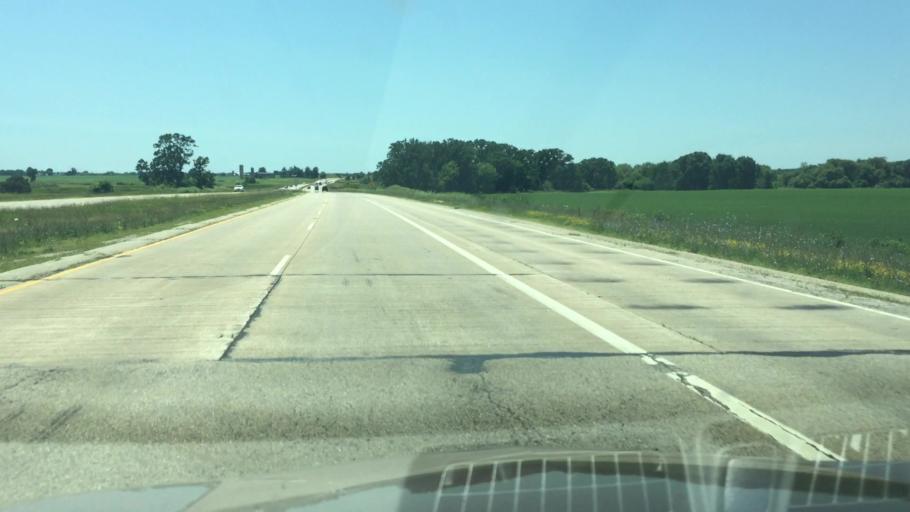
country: US
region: Wisconsin
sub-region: Fond du Lac County
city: Waupun
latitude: 43.5956
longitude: -88.7350
